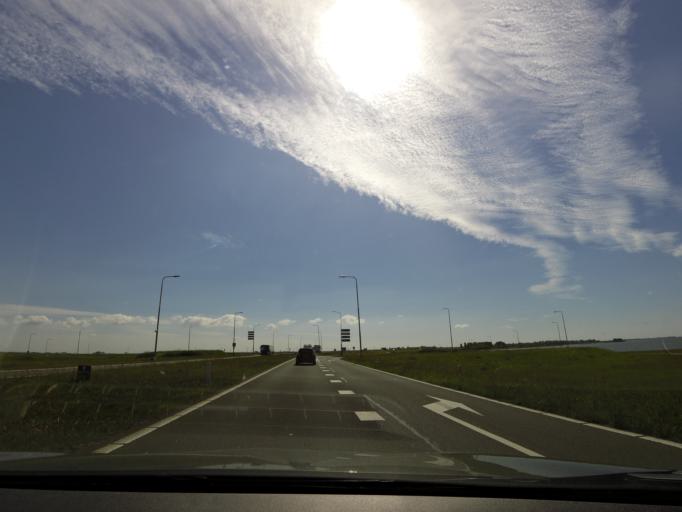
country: NL
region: Zeeland
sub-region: Schouwen-Duiveland
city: Bruinisse
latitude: 51.6821
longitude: 4.1557
